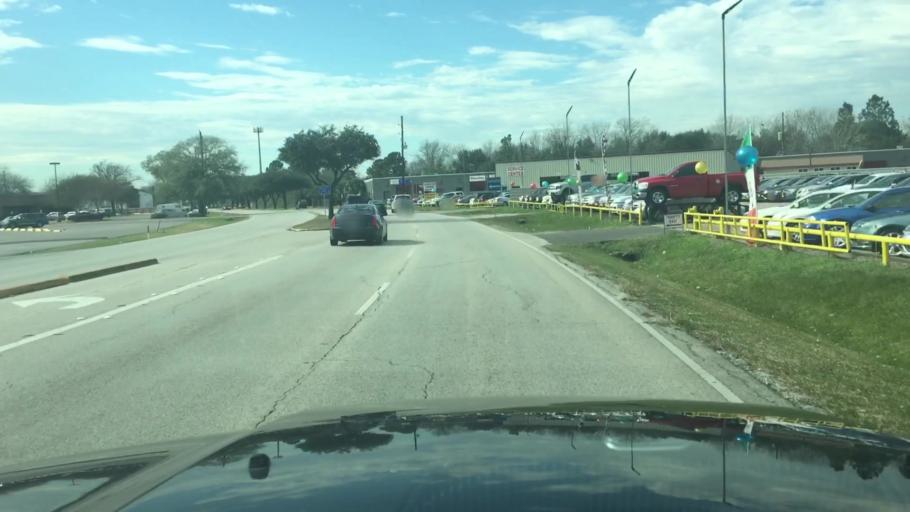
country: US
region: Texas
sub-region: Harris County
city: Oak Cliff Place
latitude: 29.8347
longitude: -95.6560
